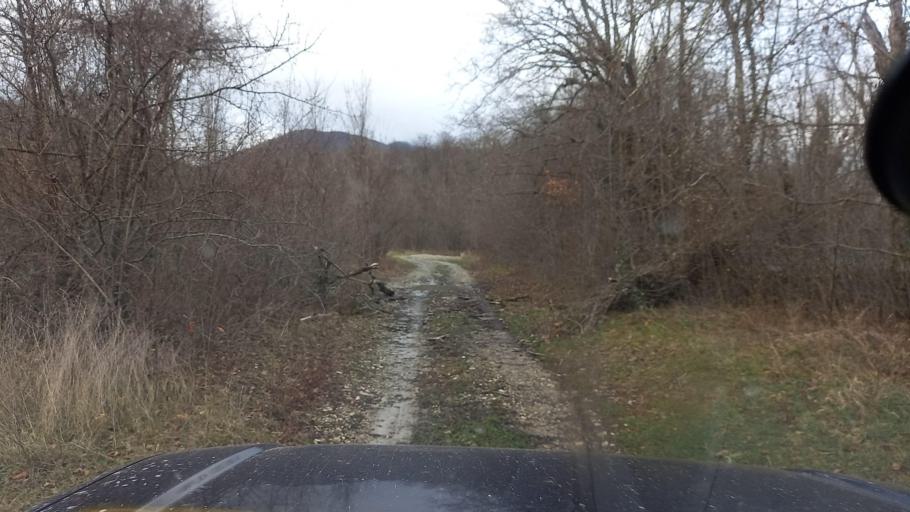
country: RU
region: Krasnodarskiy
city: Pshada
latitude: 44.4923
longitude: 38.4118
